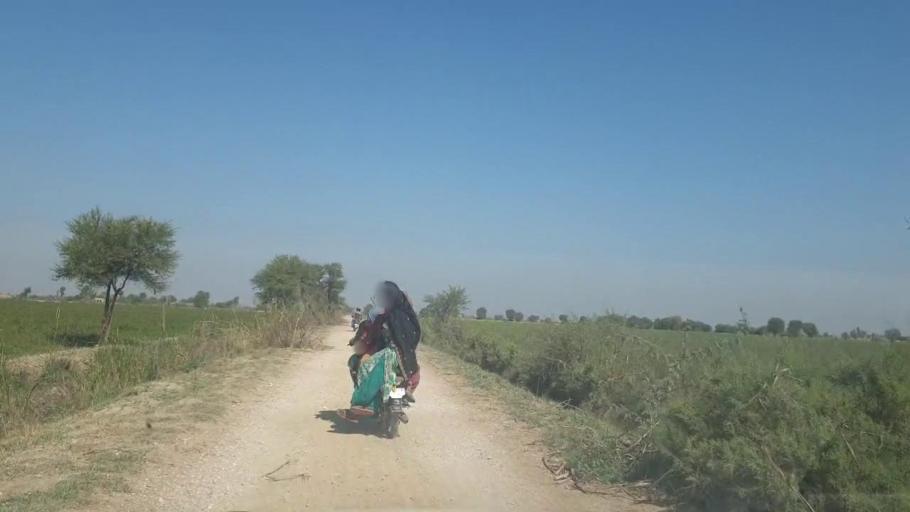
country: PK
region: Sindh
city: Mirpur Khas
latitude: 25.5544
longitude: 69.1966
